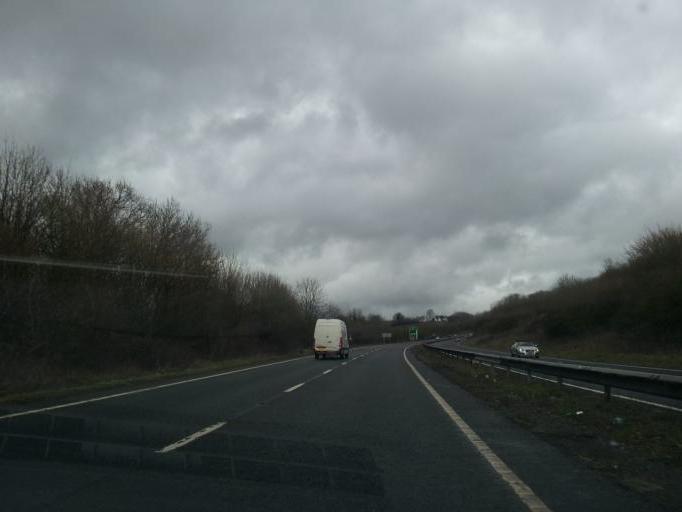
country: GB
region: England
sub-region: Somerset
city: Wincanton
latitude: 51.0660
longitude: -2.3706
